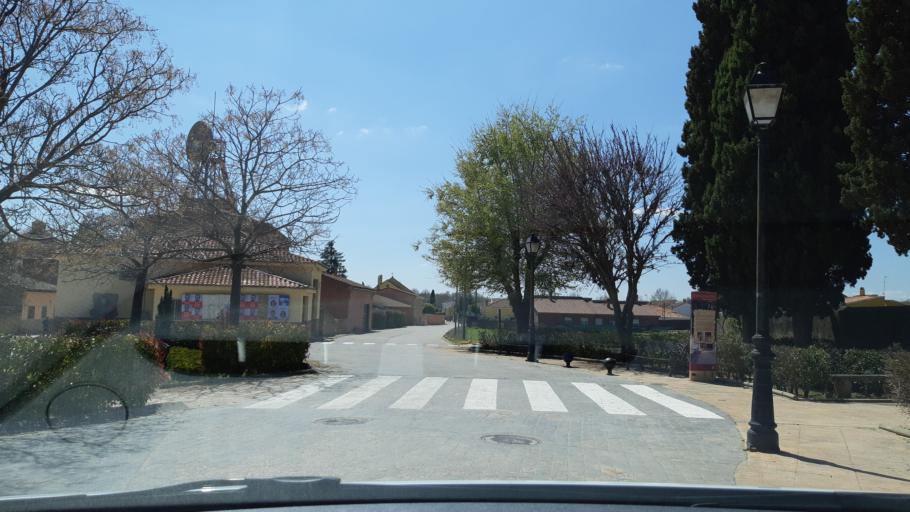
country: ES
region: Castille-La Mancha
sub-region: Provincia de Guadalajara
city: Cifuentes
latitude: 40.7878
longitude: -2.6235
